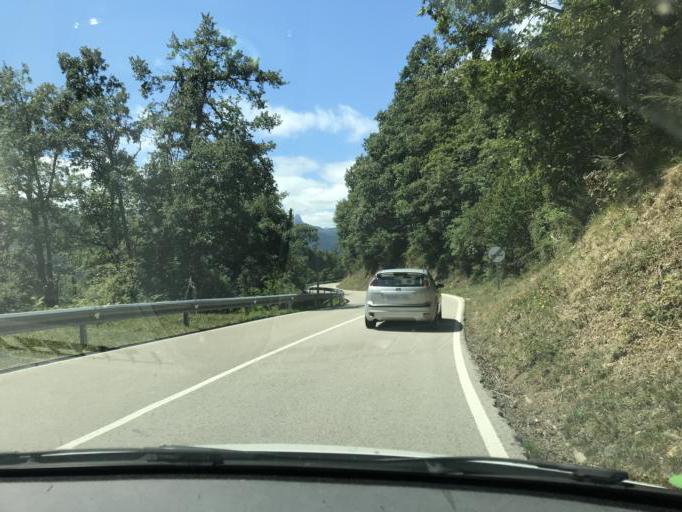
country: ES
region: Cantabria
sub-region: Provincia de Cantabria
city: Cabezon de Liebana
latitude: 43.0755
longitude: -4.4786
